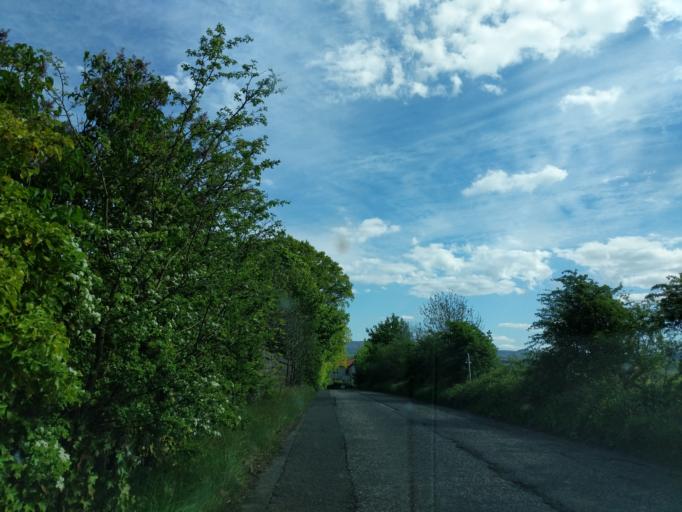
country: GB
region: Scotland
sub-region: Edinburgh
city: Ratho
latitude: 55.9345
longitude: -3.3509
